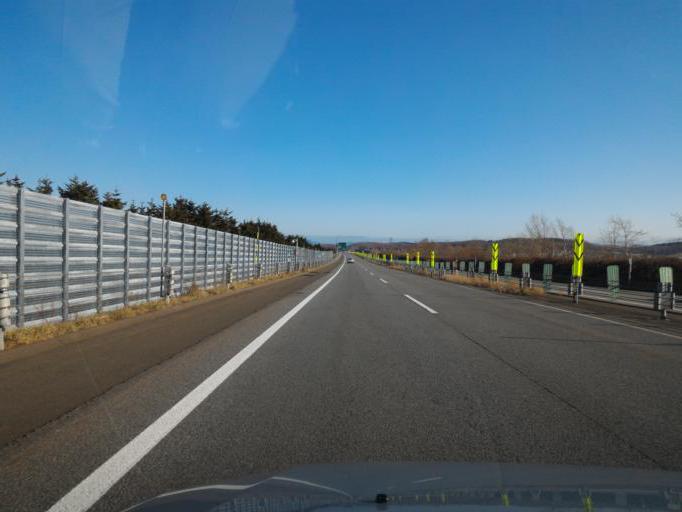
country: JP
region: Hokkaido
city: Iwamizawa
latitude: 43.1671
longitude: 141.7527
